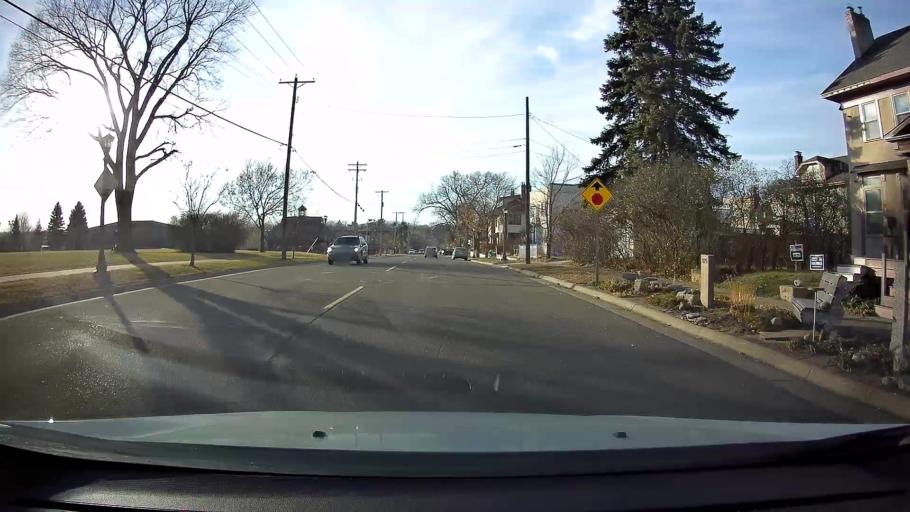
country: US
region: Minnesota
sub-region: Dakota County
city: West Saint Paul
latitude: 44.9341
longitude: -93.1349
